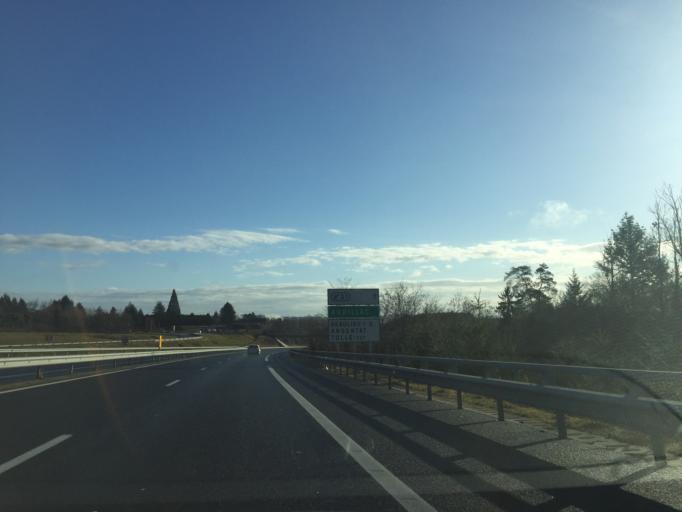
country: FR
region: Limousin
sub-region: Departement de la Correze
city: Naves
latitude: 45.3278
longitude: 1.7643
